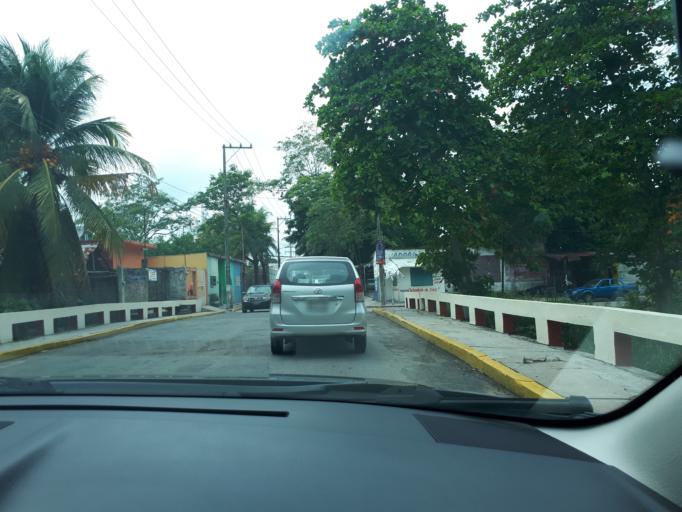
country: MX
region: Tabasco
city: Comalcalco
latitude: 18.2750
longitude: -93.2221
